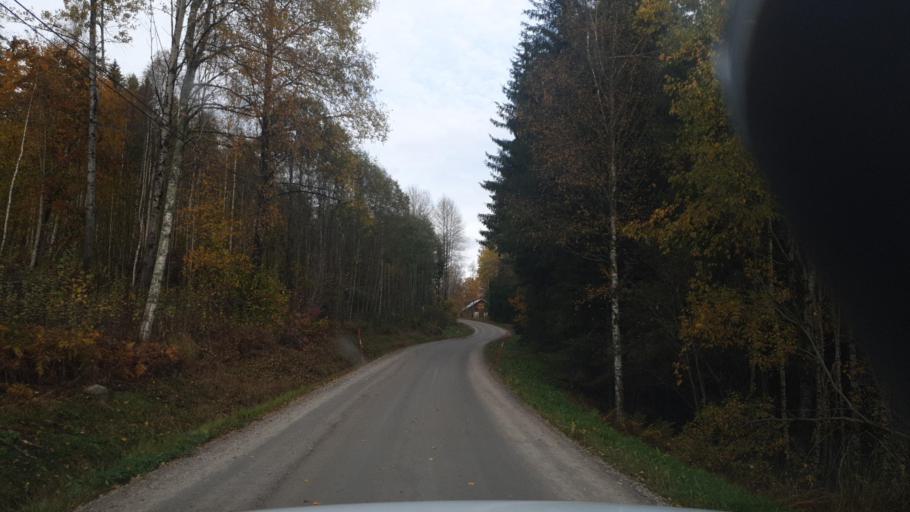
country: SE
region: Vaermland
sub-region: Sunne Kommun
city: Sunne
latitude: 59.6967
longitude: 12.8848
